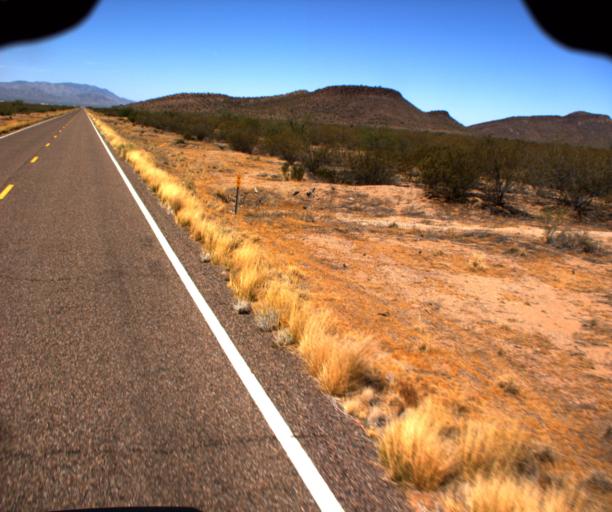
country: US
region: Arizona
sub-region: Yavapai County
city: Congress
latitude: 34.0191
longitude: -113.0979
